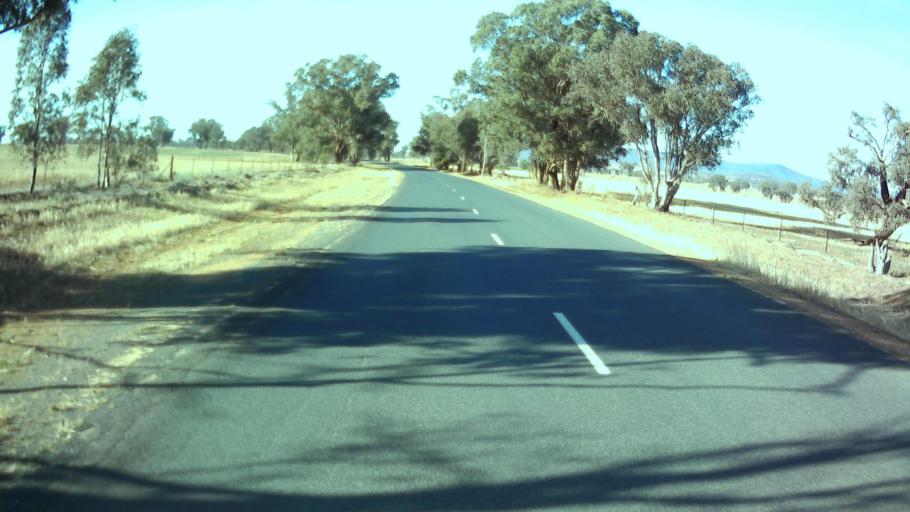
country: AU
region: New South Wales
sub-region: Weddin
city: Grenfell
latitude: -33.9233
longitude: 148.1392
